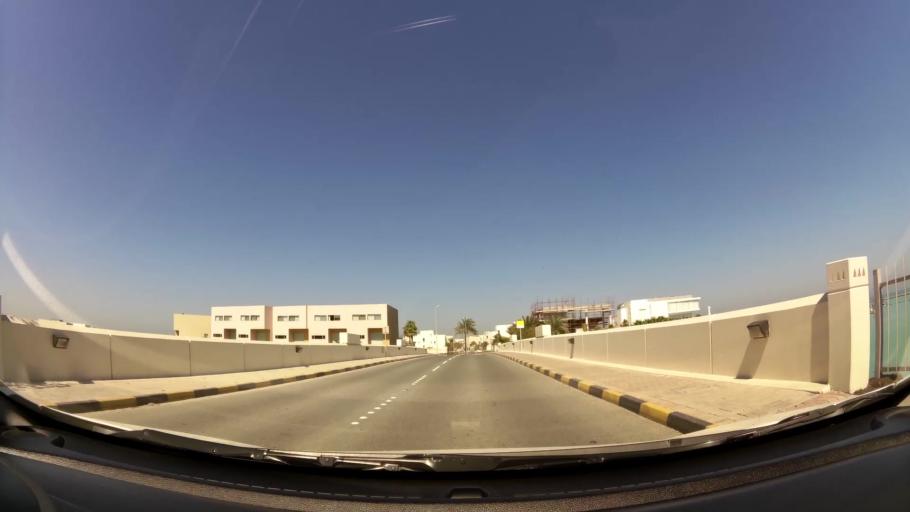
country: BH
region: Muharraq
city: Al Hadd
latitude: 26.2868
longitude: 50.6728
